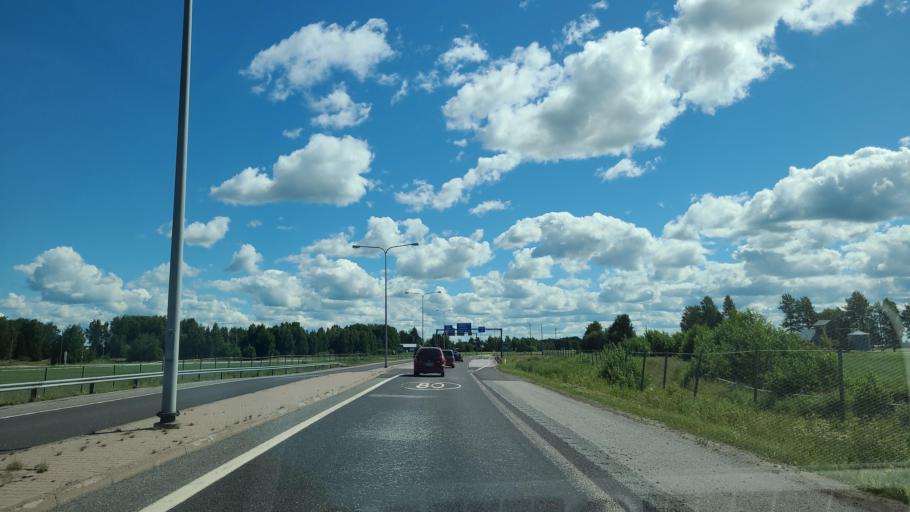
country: FI
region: Ostrobothnia
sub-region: Vaasa
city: Ristinummi
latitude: 63.0248
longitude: 21.7886
